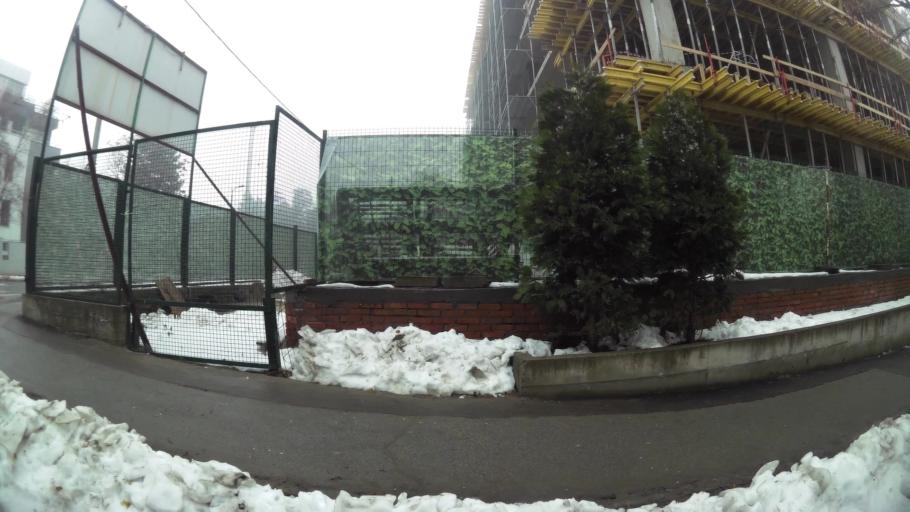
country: RS
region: Central Serbia
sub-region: Belgrade
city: Savski Venac
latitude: 44.7732
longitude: 20.4625
